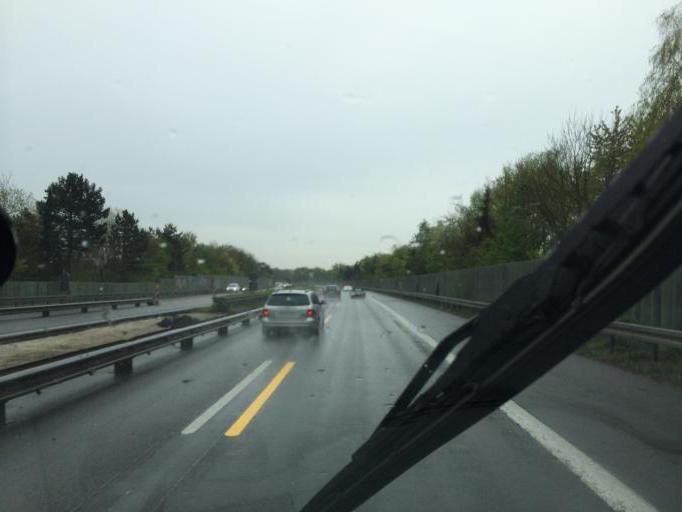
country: DE
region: North Rhine-Westphalia
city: Marl
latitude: 51.6685
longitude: 7.1567
